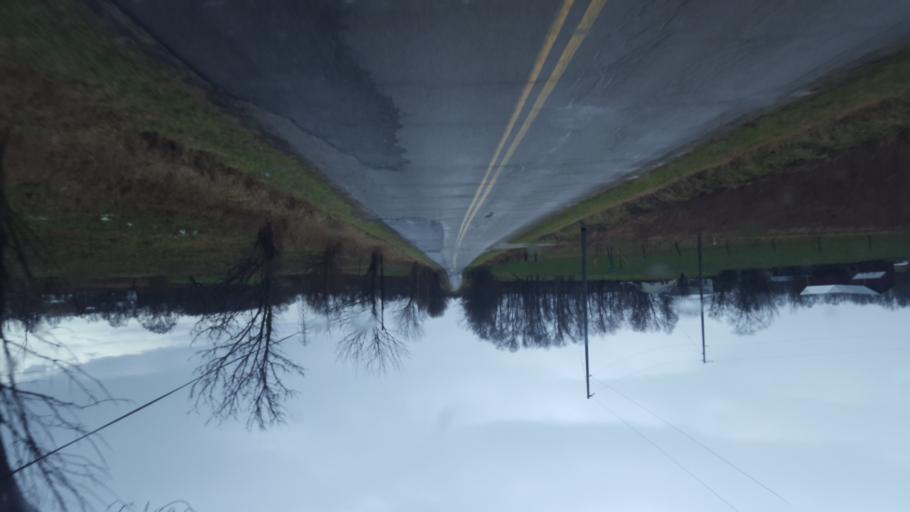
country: US
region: Ohio
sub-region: Knox County
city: Fredericktown
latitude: 40.5231
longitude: -82.4107
